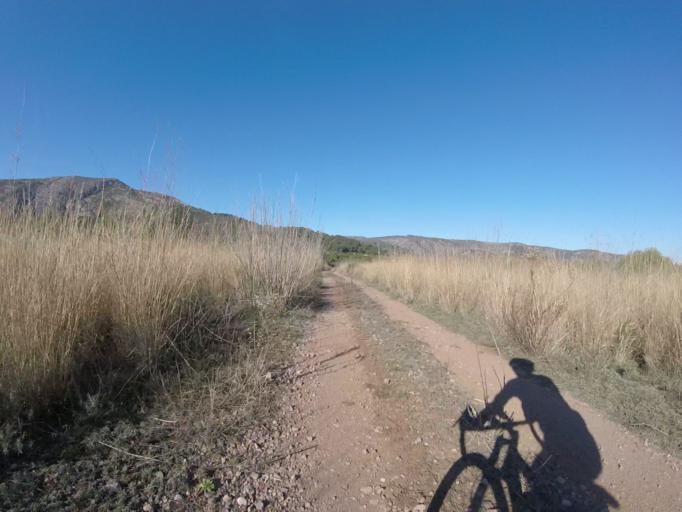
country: ES
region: Valencia
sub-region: Provincia de Castello
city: Orpesa/Oropesa del Mar
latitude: 40.1229
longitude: 0.1134
